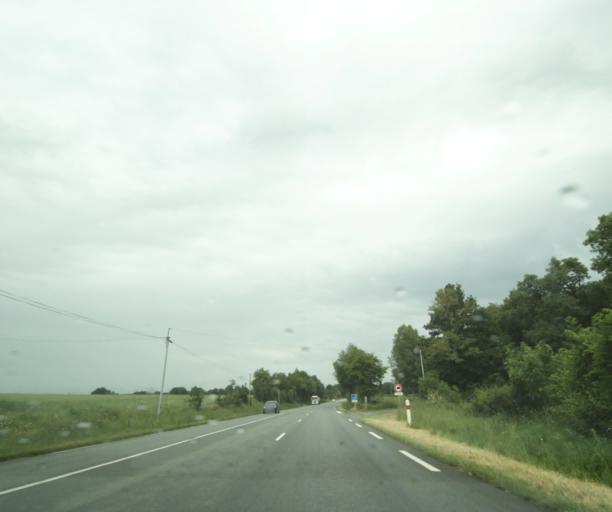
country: FR
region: Poitou-Charentes
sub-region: Departement des Deux-Sevres
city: Le Tallud
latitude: 46.6189
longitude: -0.2823
